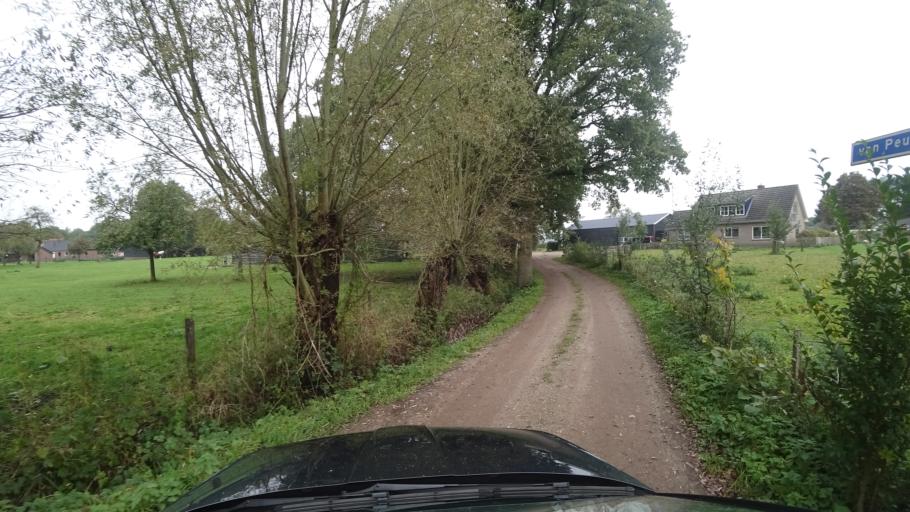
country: NL
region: Gelderland
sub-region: Gemeente Ede
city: Ede
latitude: 52.0592
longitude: 5.6438
